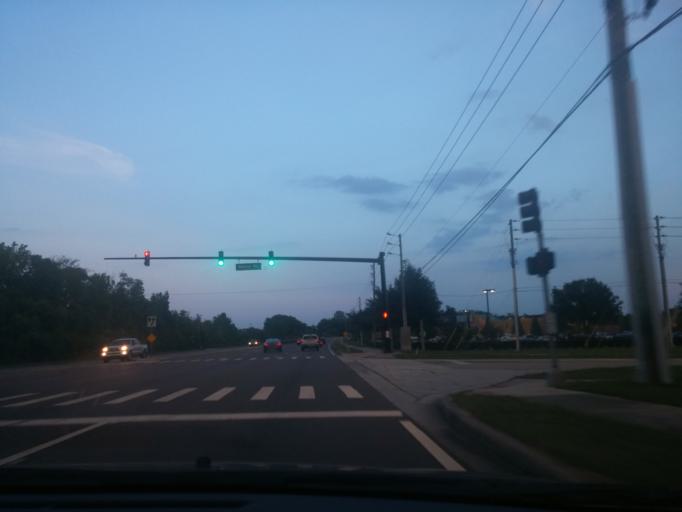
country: US
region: Florida
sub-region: Seminole County
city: Oviedo
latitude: 28.6478
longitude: -81.2503
